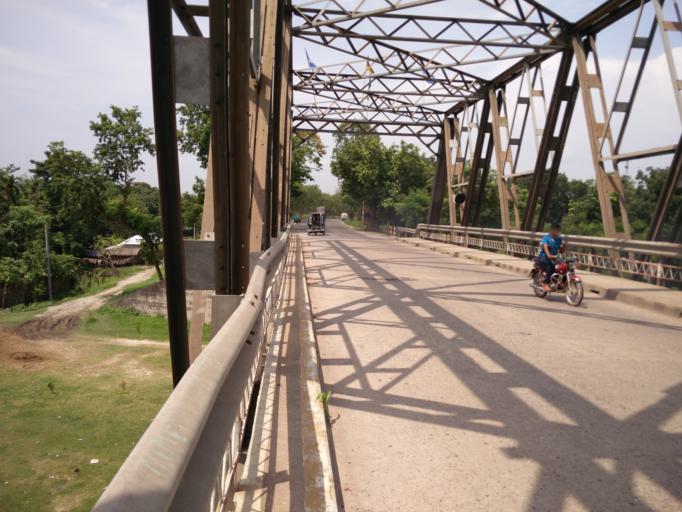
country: BD
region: Khulna
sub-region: Magura
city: Magura
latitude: 23.5396
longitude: 89.5161
